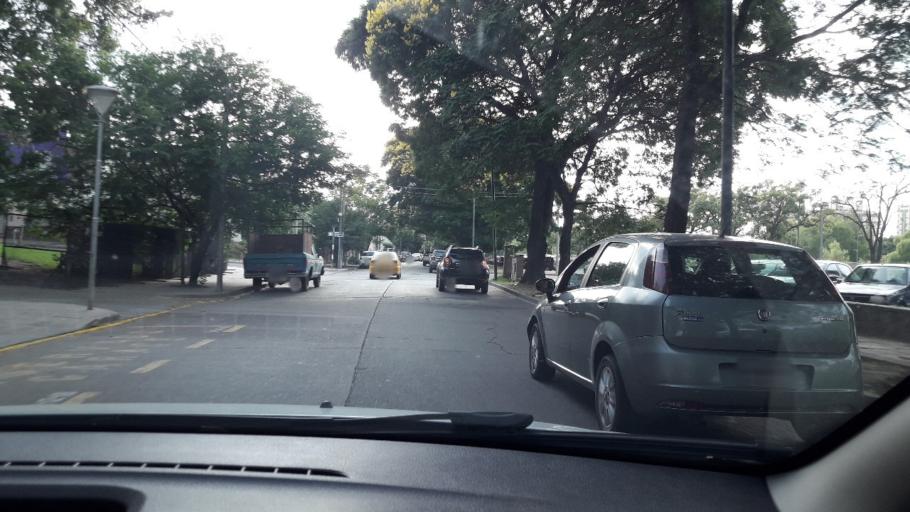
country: AR
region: Jujuy
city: San Salvador de Jujuy
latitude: -24.1885
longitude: -65.2979
